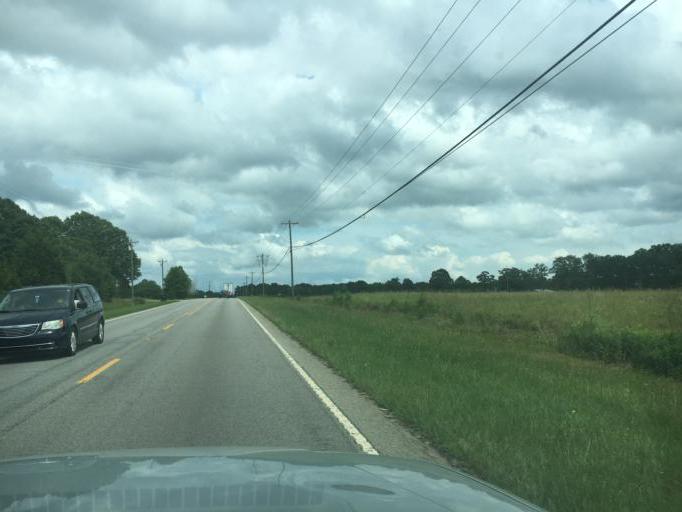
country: US
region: South Carolina
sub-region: Anderson County
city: Williamston
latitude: 34.6312
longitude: -82.4031
